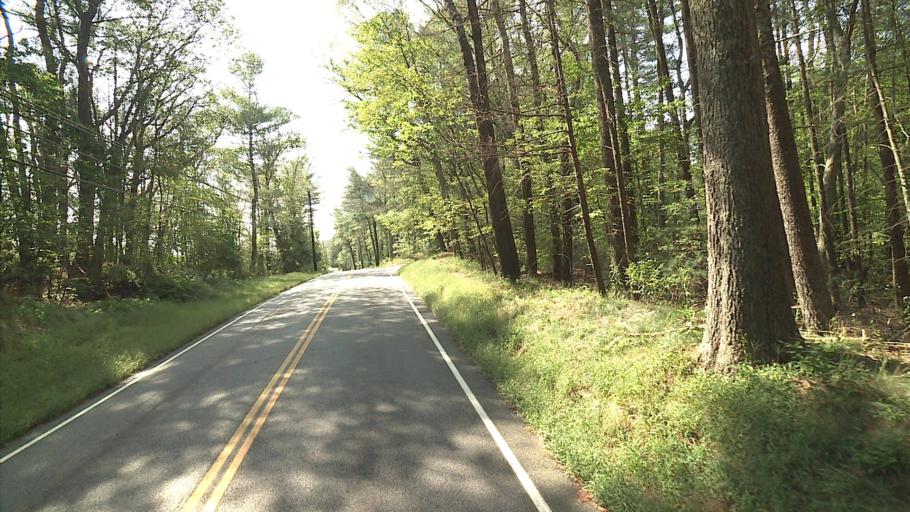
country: US
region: Connecticut
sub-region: Windham County
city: Wauregan
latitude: 41.7718
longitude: -71.9546
